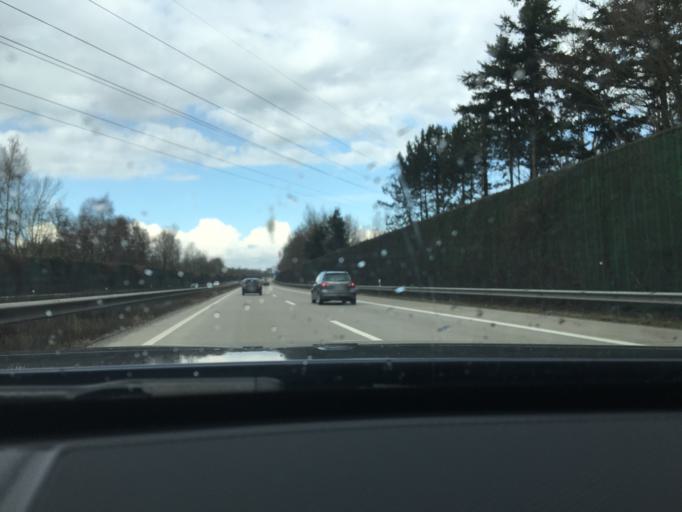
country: DE
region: Lower Saxony
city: Schiffdorf
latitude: 53.5306
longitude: 8.6223
